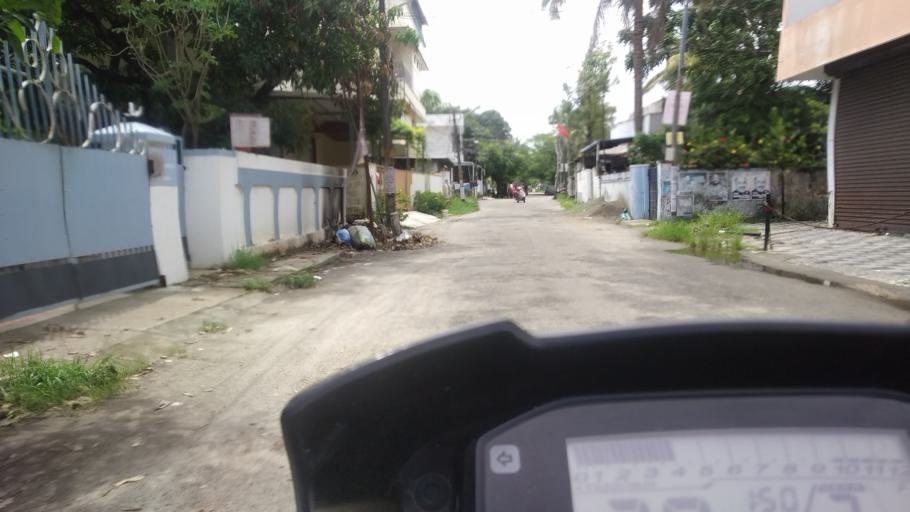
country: IN
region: Kerala
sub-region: Ernakulam
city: Elur
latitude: 10.0056
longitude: 76.2836
